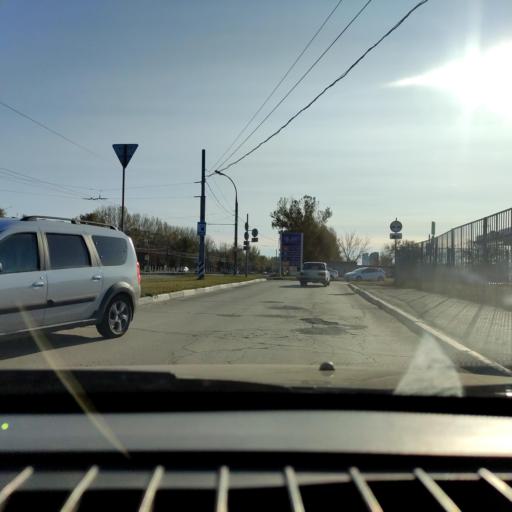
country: RU
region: Samara
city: Tol'yatti
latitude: 53.5302
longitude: 49.2609
